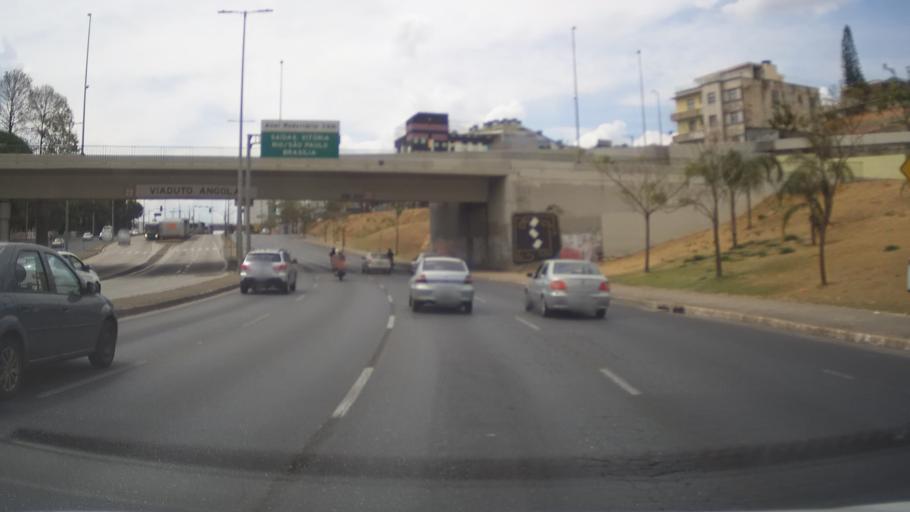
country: BR
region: Minas Gerais
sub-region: Belo Horizonte
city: Belo Horizonte
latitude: -19.9028
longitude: -43.9446
